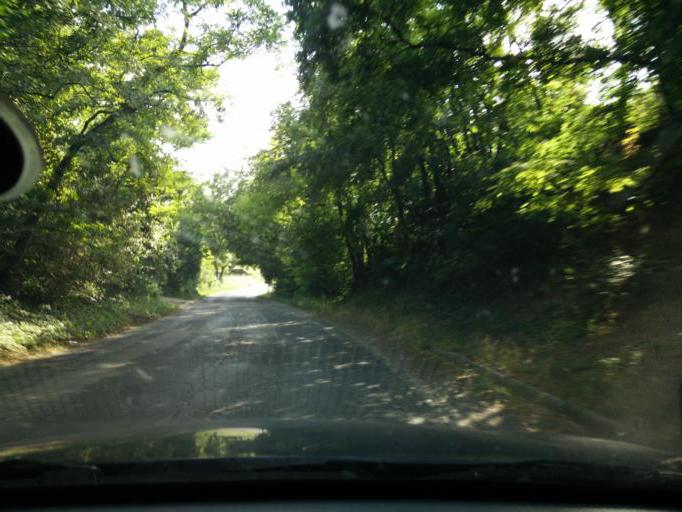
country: HU
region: Komarom-Esztergom
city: Baj
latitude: 47.6669
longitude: 18.3799
